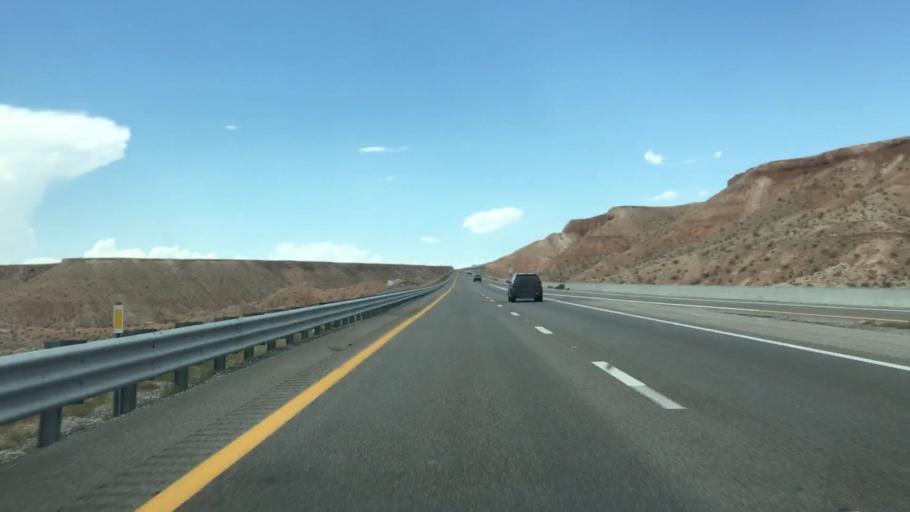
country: US
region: Nevada
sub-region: Clark County
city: Bunkerville
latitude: 36.7732
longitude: -114.2412
